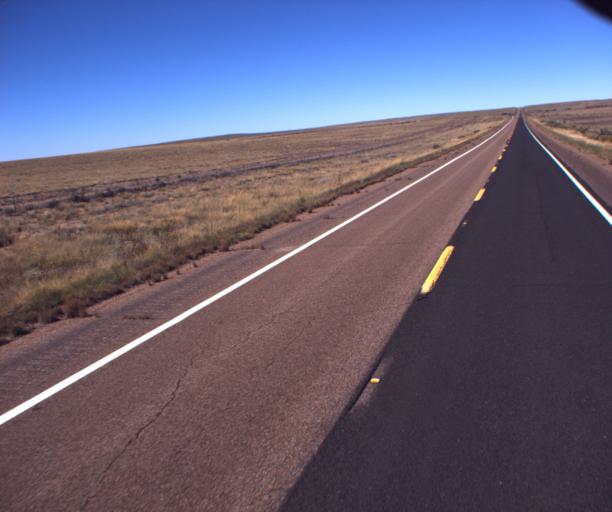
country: US
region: Arizona
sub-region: Navajo County
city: Snowflake
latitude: 34.7299
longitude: -109.7816
